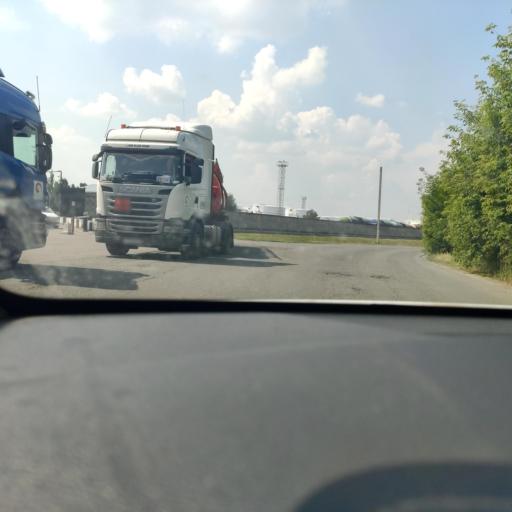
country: RU
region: Tatarstan
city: Stolbishchi
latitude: 55.6160
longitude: 49.2786
